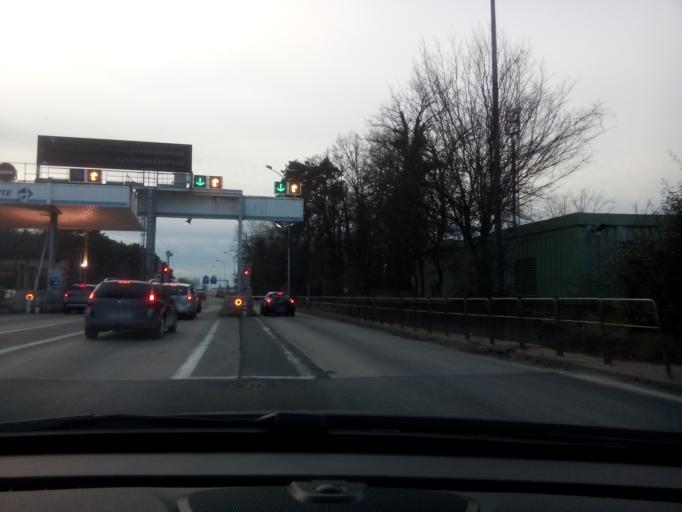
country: FR
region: Centre
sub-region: Departement du Loiret
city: Saran
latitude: 47.9495
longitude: 1.8551
